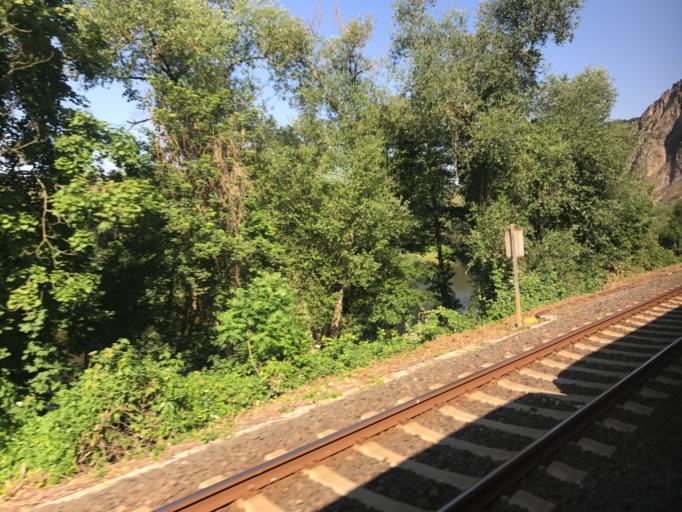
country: DE
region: Rheinland-Pfalz
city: Bad Munster am Stein-Ebernburg
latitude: 49.8131
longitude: 7.8377
